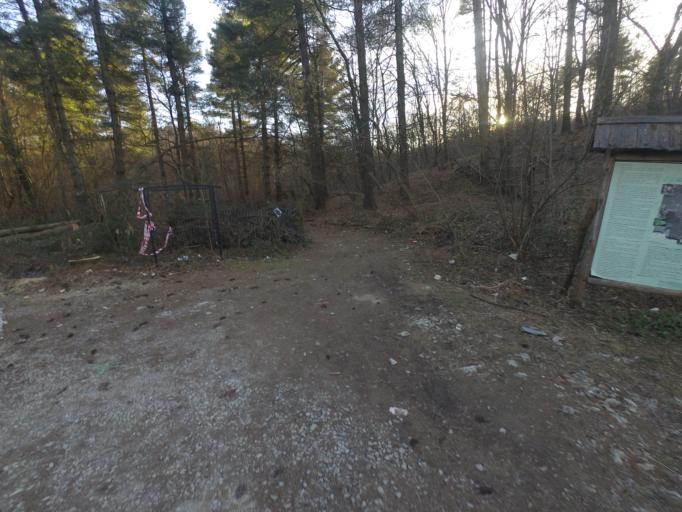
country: HR
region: Karlovacka
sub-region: Grad Karlovac
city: Karlovac
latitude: 45.4779
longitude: 15.5336
